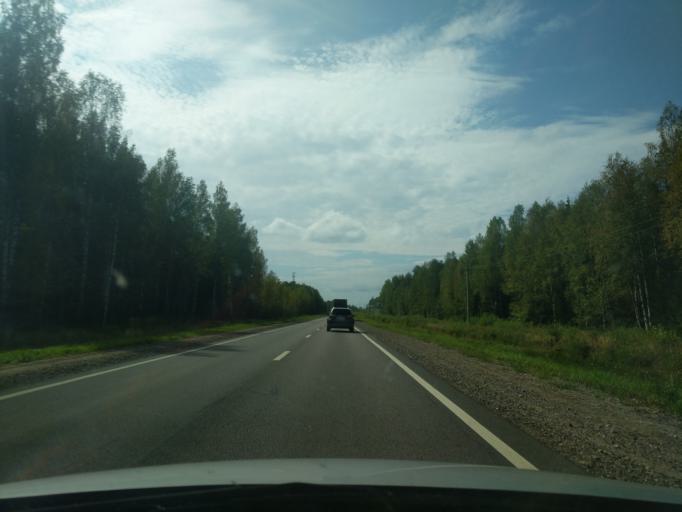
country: RU
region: Kostroma
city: Kadyy
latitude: 57.8036
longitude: 43.2118
